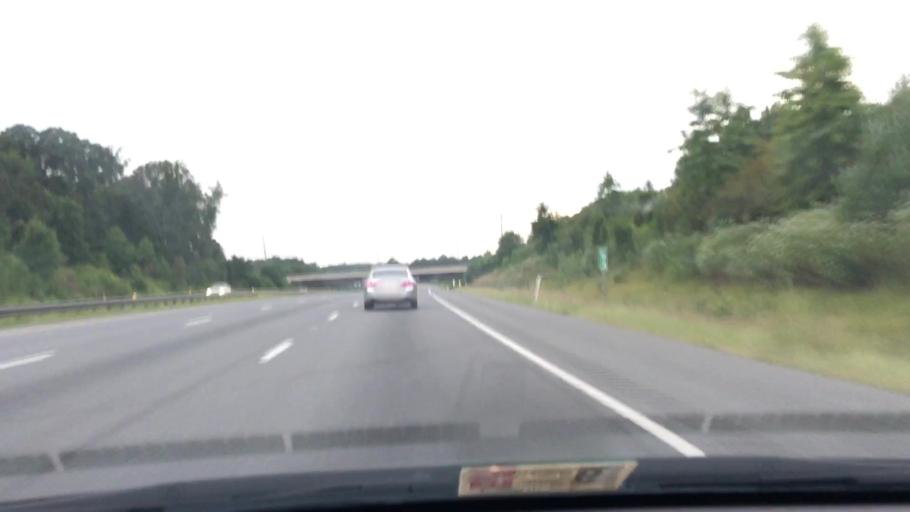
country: US
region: Maryland
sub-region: Montgomery County
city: Leisure World
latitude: 39.1104
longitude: -77.0579
